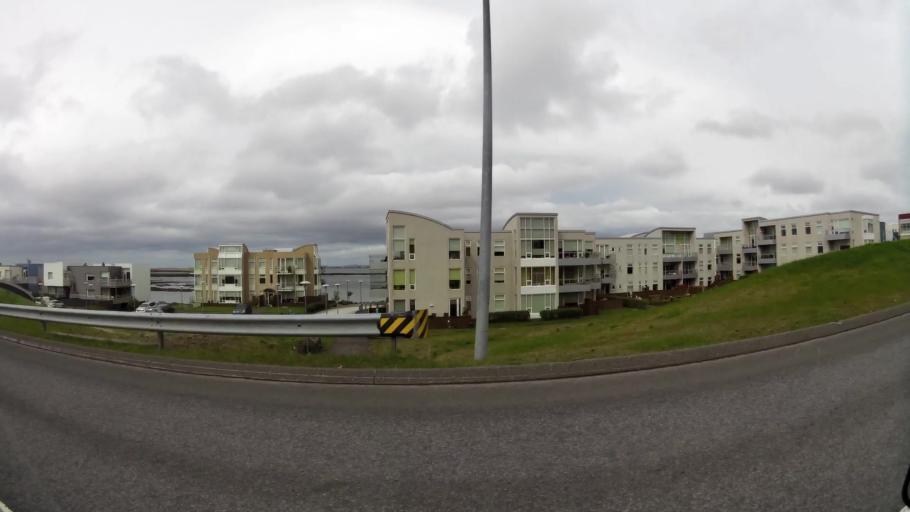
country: IS
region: Capital Region
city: Gardabaer
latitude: 64.0921
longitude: -21.9478
